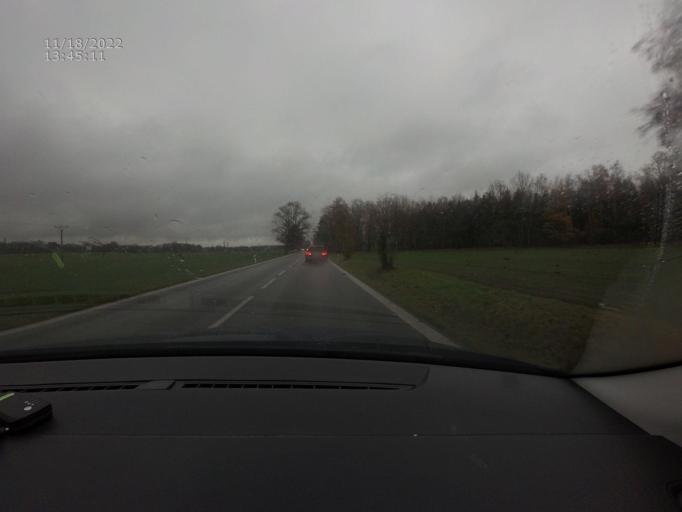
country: CZ
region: Jihocesky
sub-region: Okres Strakonice
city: Blatna
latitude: 49.4290
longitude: 13.8427
